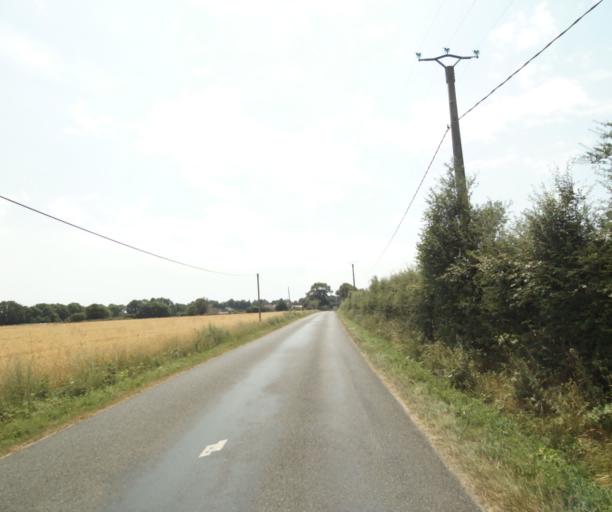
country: FR
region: Centre
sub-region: Departement d'Eure-et-Loir
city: La Bazoche-Gouet
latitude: 48.1791
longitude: 1.0140
